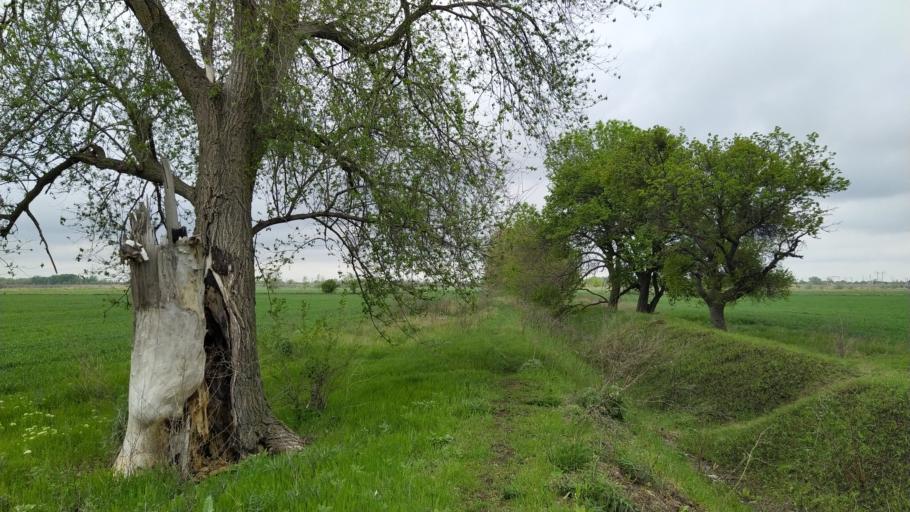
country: RU
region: Rostov
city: Bataysk
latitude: 47.1239
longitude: 39.7249
